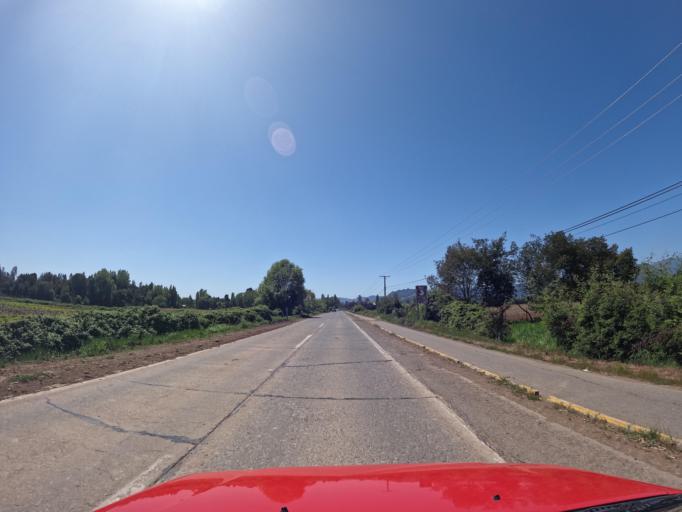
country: CL
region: Maule
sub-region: Provincia de Linares
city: Colbun
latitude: -35.7699
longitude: -71.4268
